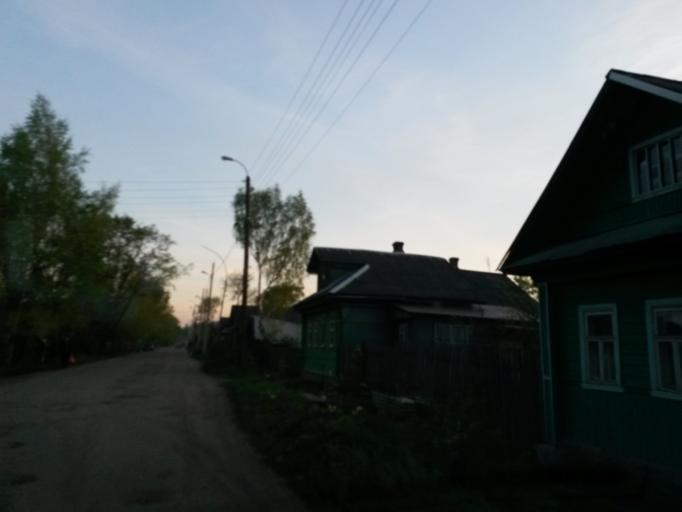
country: RU
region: Jaroslavl
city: Tutayev
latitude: 57.8873
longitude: 39.5517
